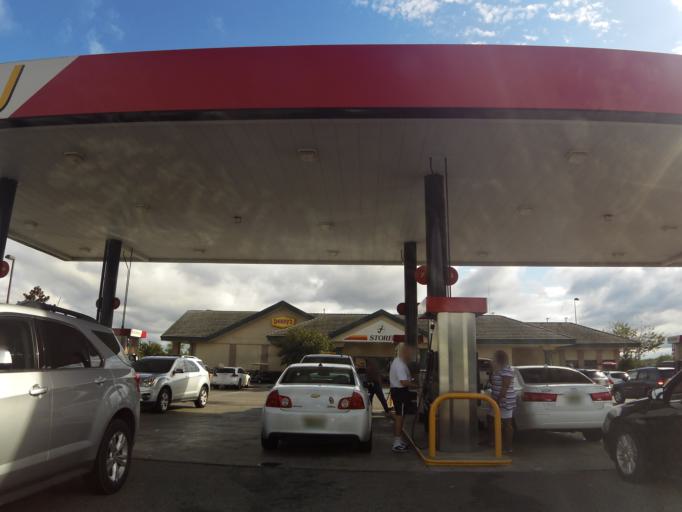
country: US
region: Alabama
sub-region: Lowndes County
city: Hayneville
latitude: 32.1948
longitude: -86.4196
